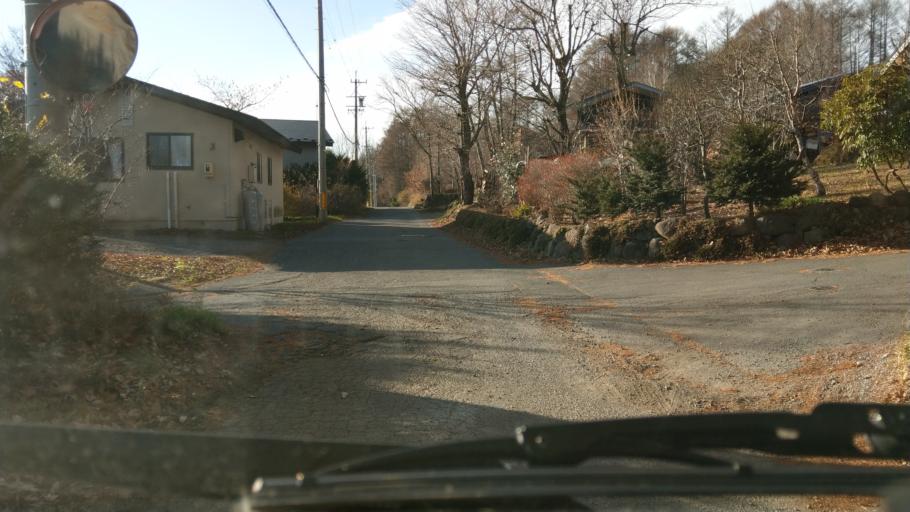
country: JP
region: Nagano
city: Komoro
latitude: 36.3441
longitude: 138.4574
